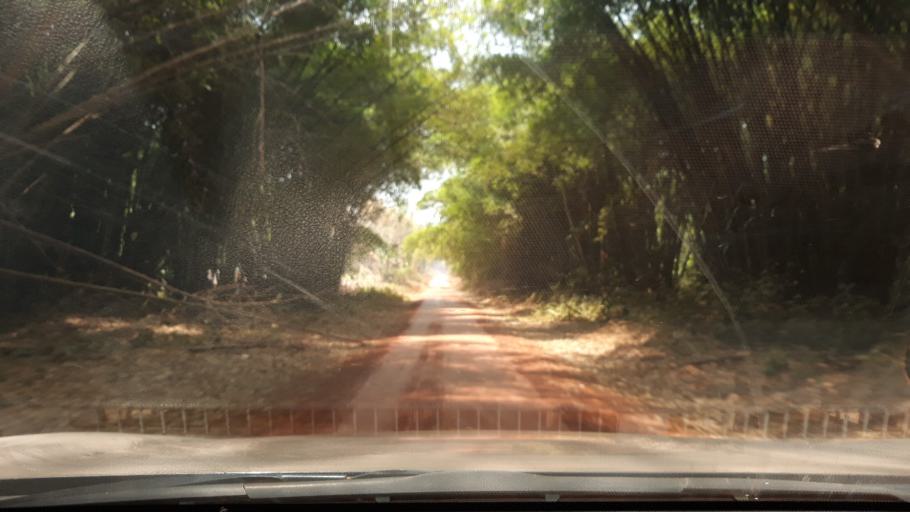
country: CD
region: Eastern Province
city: Buta
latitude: 2.2838
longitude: 25.1157
